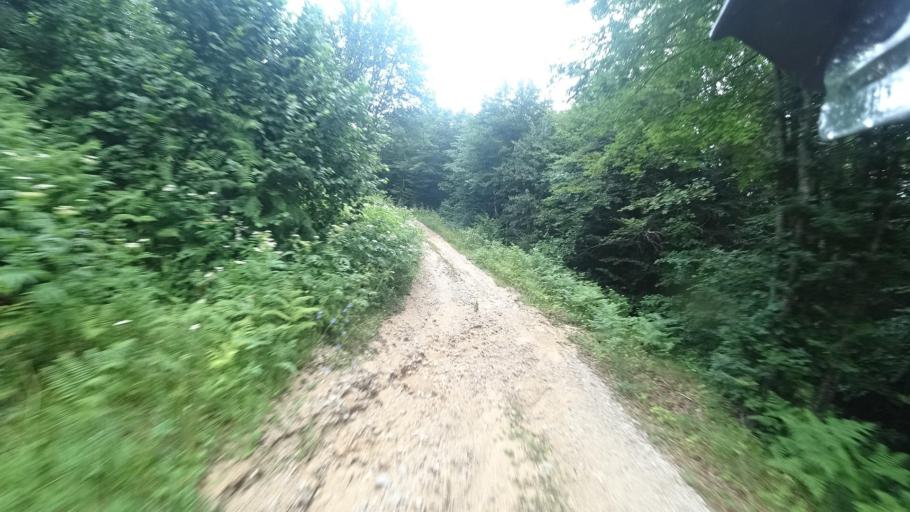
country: HR
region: Licko-Senjska
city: Jezerce
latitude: 44.7470
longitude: 15.6298
